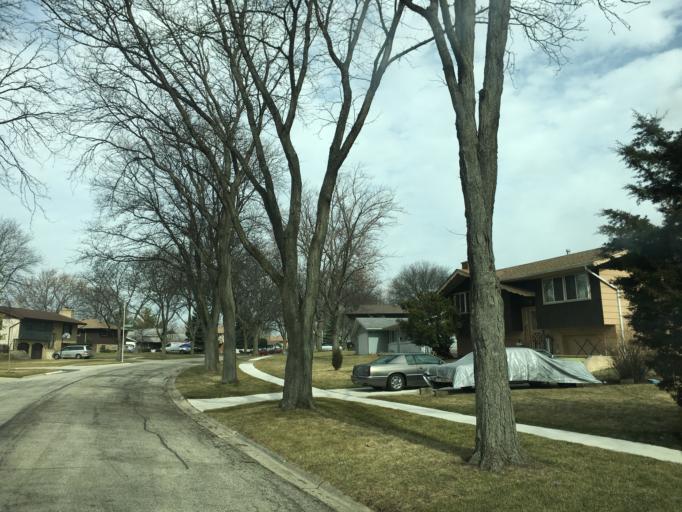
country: US
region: Illinois
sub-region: DuPage County
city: Hanover Park
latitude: 42.0010
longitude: -88.1214
